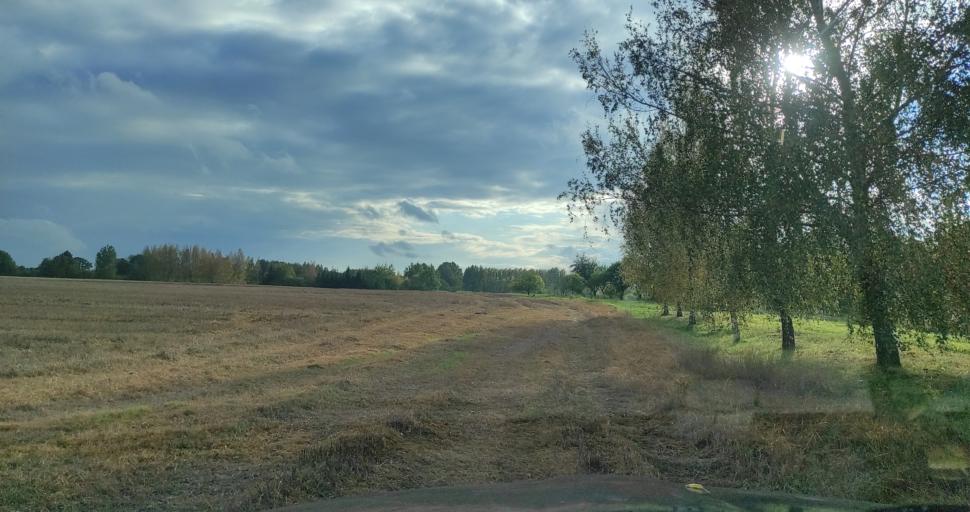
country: LV
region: Talsu Rajons
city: Sabile
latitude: 56.9007
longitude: 22.4210
